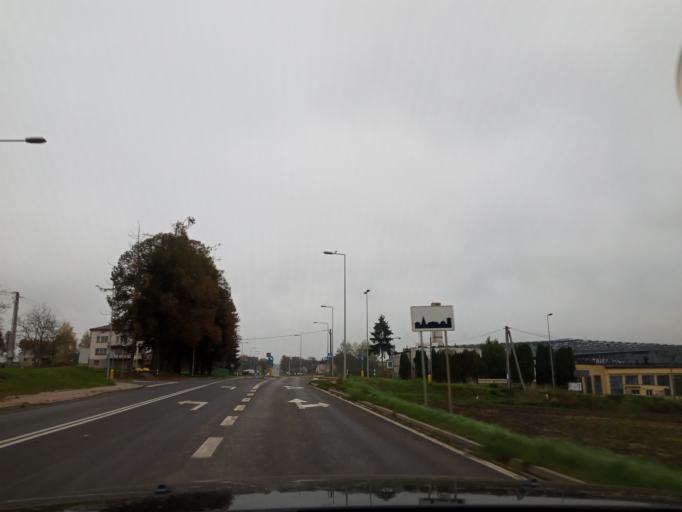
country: PL
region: Lesser Poland Voivodeship
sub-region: Powiat proszowicki
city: Proszowice
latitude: 50.2032
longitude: 20.3037
